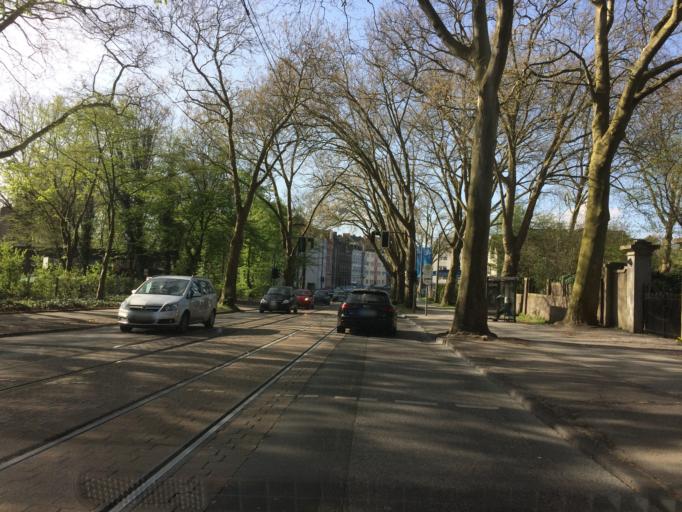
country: DE
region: North Rhine-Westphalia
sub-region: Regierungsbezirk Munster
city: Gelsenkirchen
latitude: 51.4952
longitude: 7.1159
